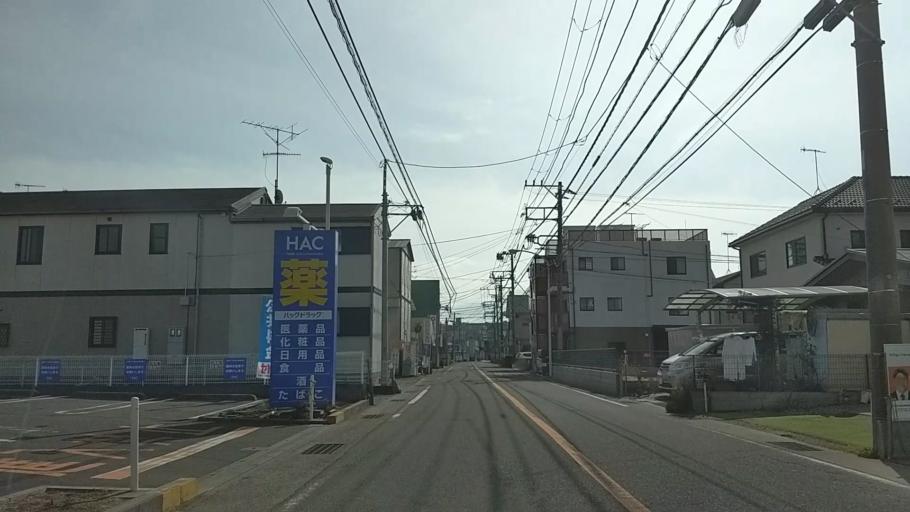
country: JP
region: Kanagawa
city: Chigasaki
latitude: 35.3376
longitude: 139.3829
